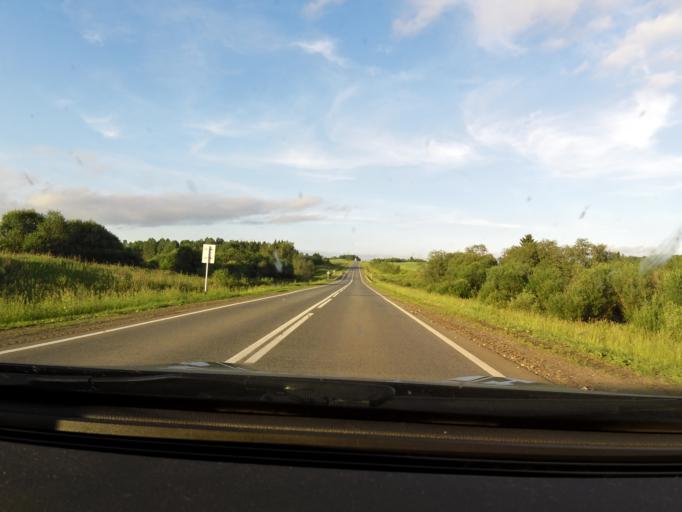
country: RU
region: Perm
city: Siva
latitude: 58.4871
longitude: 54.0943
